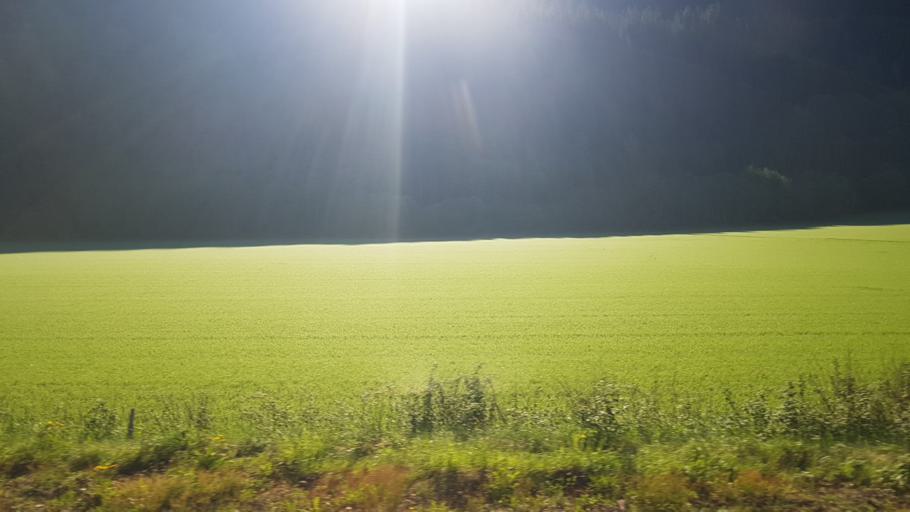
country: NO
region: Sor-Trondelag
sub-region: Melhus
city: Melhus
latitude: 63.2551
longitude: 10.2791
